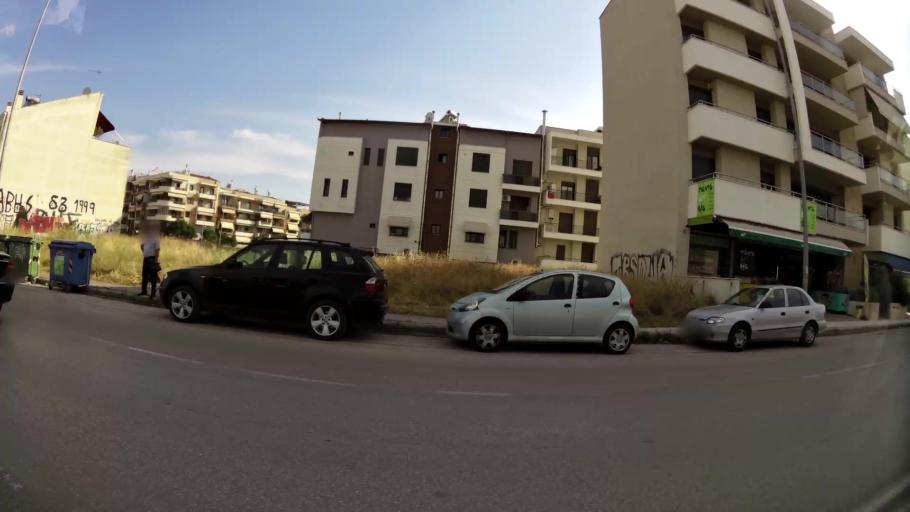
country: GR
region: Central Macedonia
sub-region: Nomos Thessalonikis
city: Kalamaria
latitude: 40.5761
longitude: 22.9665
